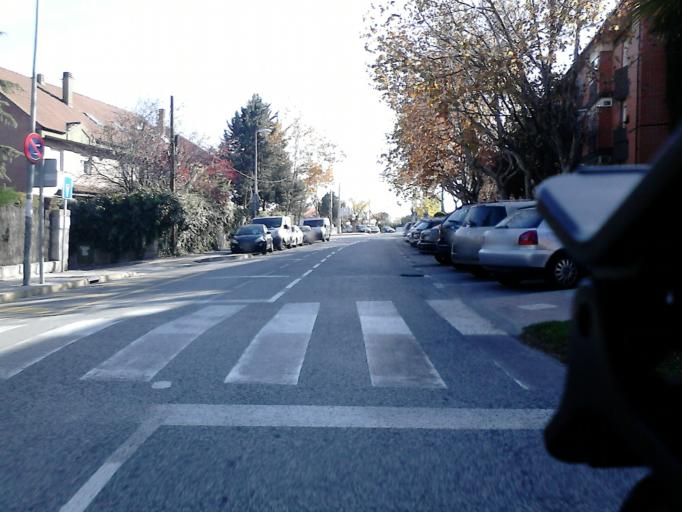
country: ES
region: Madrid
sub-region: Provincia de Madrid
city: Torrelodones
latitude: 40.5738
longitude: -3.9235
